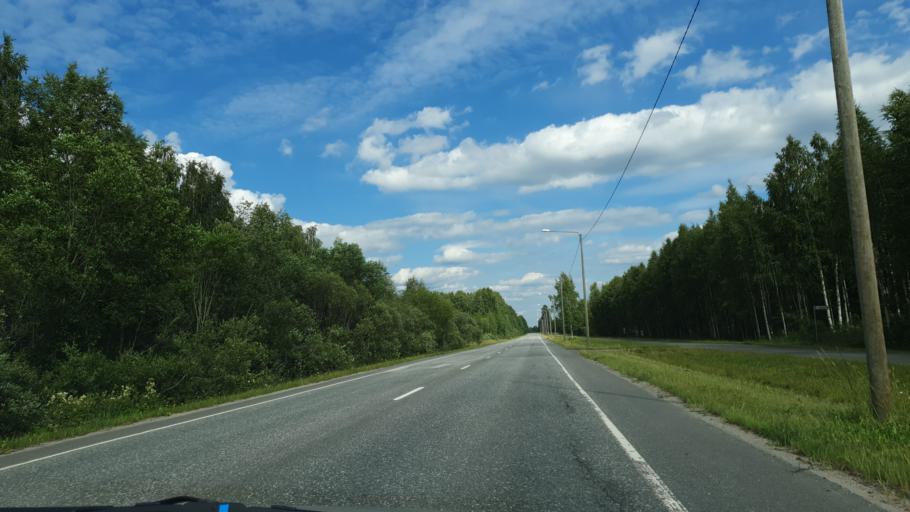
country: FI
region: Kainuu
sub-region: Kajaani
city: Kajaani
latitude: 64.2526
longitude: 27.7932
